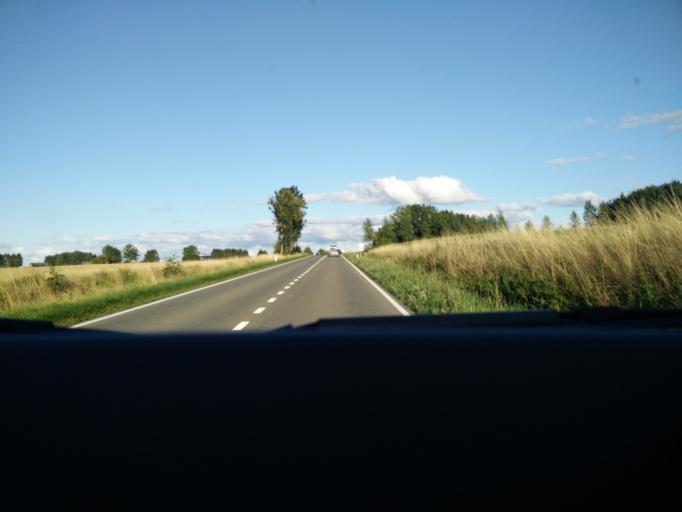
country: BE
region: Wallonia
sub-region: Province de Namur
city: Hastiere-Lavaux
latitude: 50.2363
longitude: 4.7305
